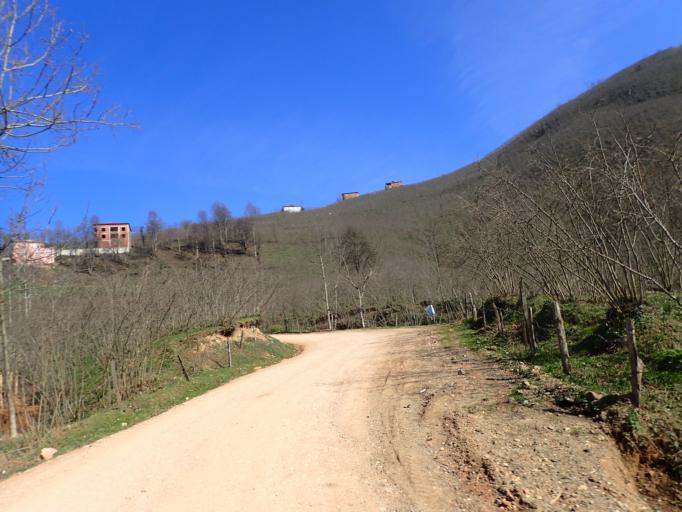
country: TR
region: Ordu
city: Catalpinar
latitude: 40.8635
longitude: 37.4967
